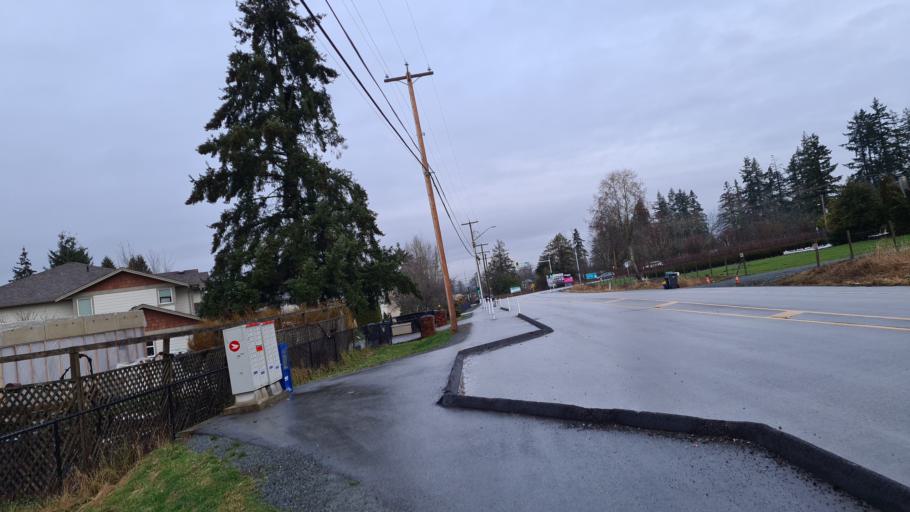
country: CA
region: British Columbia
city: Walnut Grove
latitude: 49.1468
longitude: -122.6615
